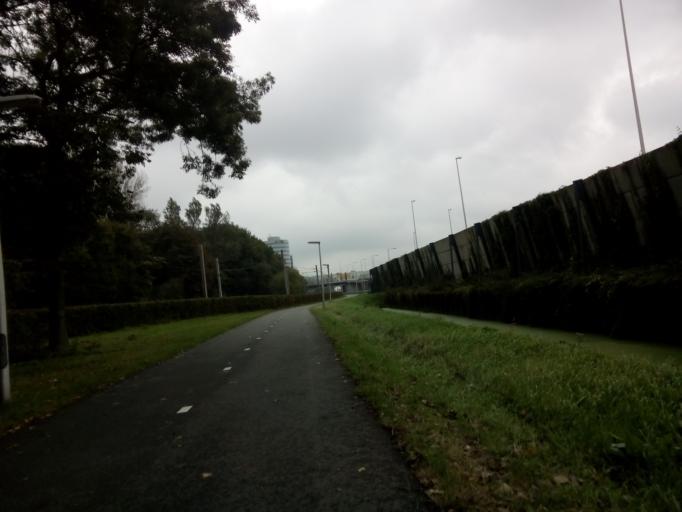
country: NL
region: South Holland
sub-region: Gemeente Zoetermeer
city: Zoetermeer
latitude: 52.0489
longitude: 4.4700
